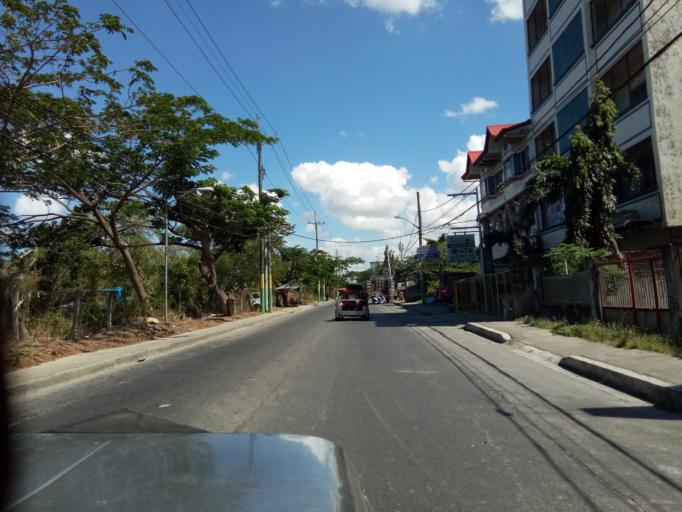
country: PH
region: Calabarzon
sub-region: Province of Cavite
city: Dasmarinas
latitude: 14.3454
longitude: 120.9464
